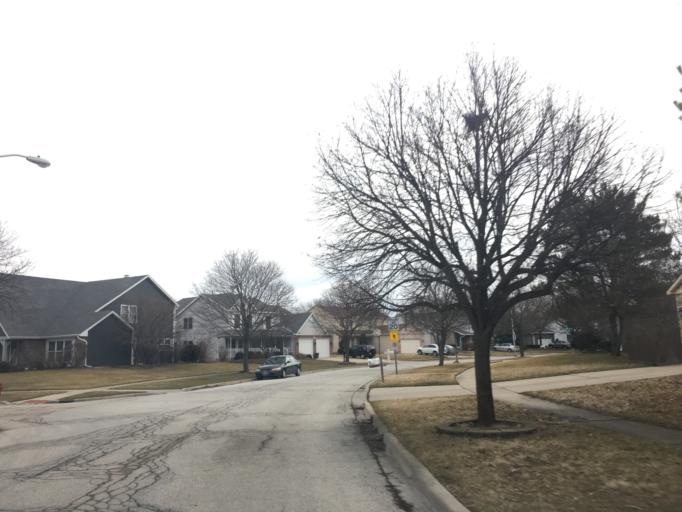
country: US
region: Illinois
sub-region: Cook County
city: Schaumburg
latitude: 42.0400
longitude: -88.1125
